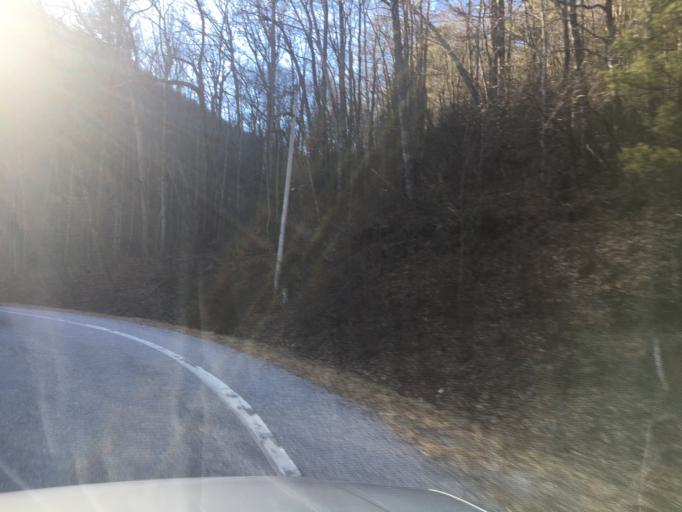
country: US
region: Georgia
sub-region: Union County
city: Blairsville
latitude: 34.7316
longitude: -83.9226
